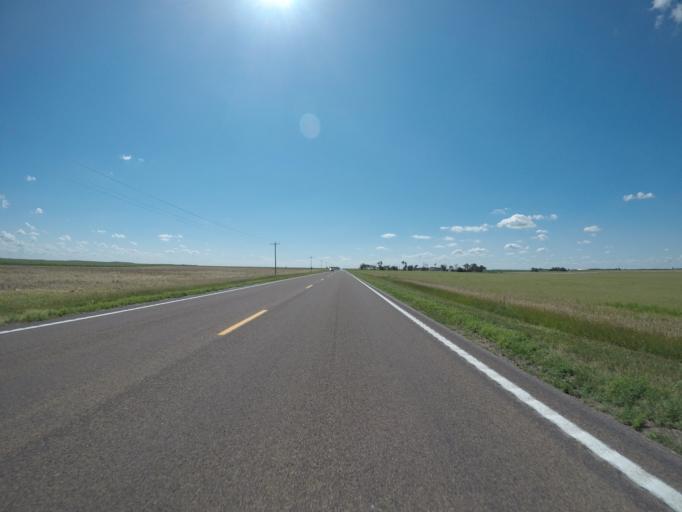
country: US
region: Nebraska
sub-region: Chase County
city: Imperial
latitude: 40.5377
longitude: -101.7039
